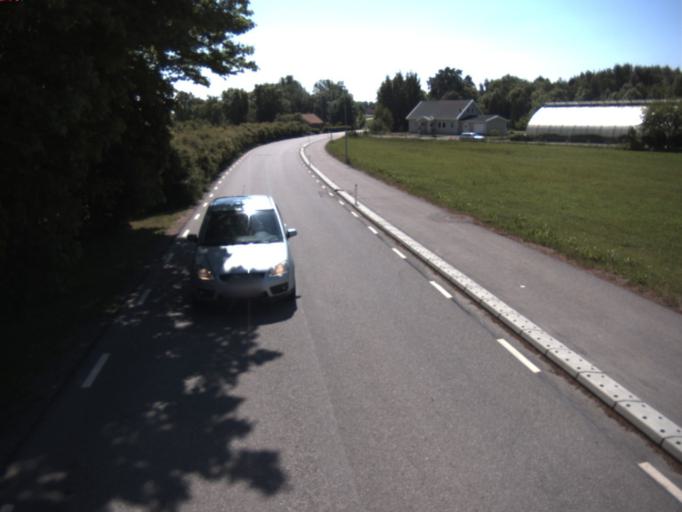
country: SE
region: Skane
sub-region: Helsingborg
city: Barslov
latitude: 56.0241
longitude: 12.8029
